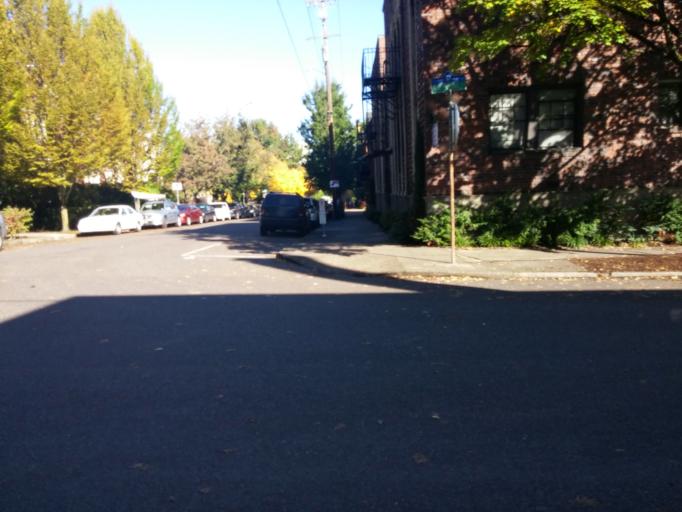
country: US
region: Oregon
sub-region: Multnomah County
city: Portland
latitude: 45.5278
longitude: -122.6923
